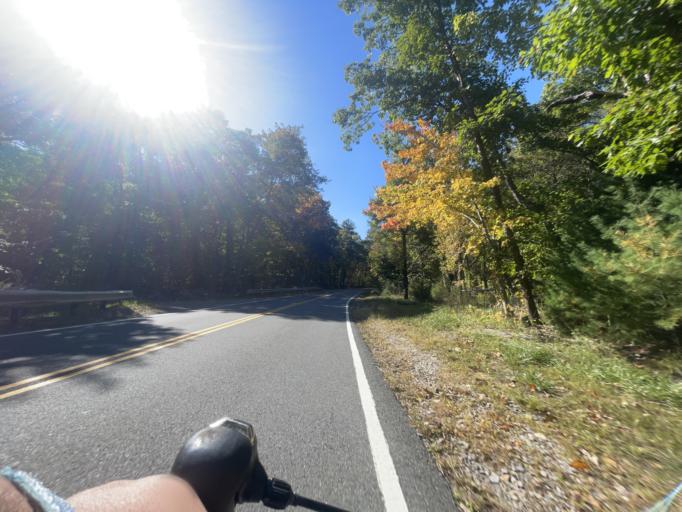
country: US
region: Massachusetts
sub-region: Norfolk County
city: Milton
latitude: 42.2282
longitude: -71.0534
